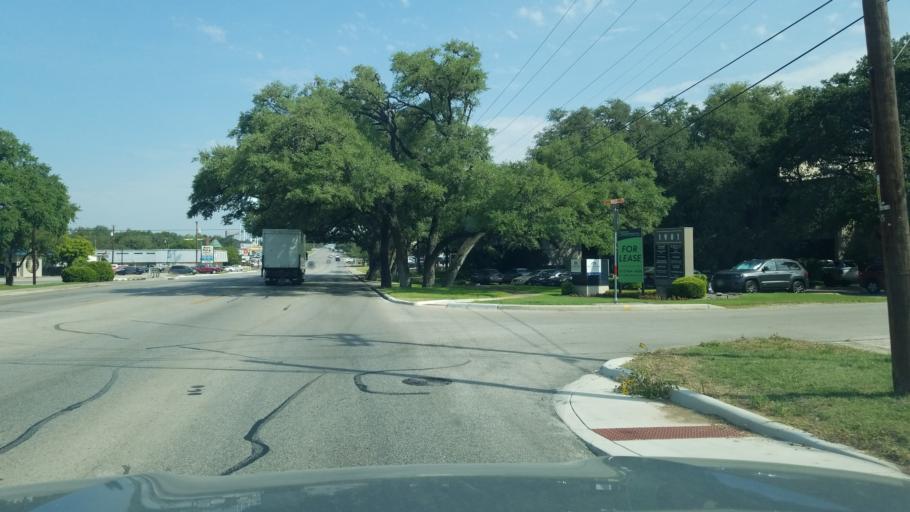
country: US
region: Texas
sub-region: Bexar County
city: Castle Hills
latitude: 29.5275
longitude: -98.5185
